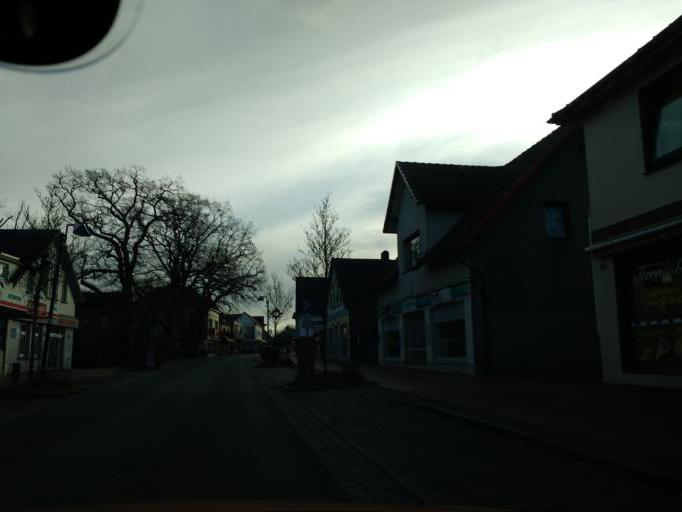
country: DE
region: Lower Saxony
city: Hude
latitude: 53.1121
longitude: 8.4587
